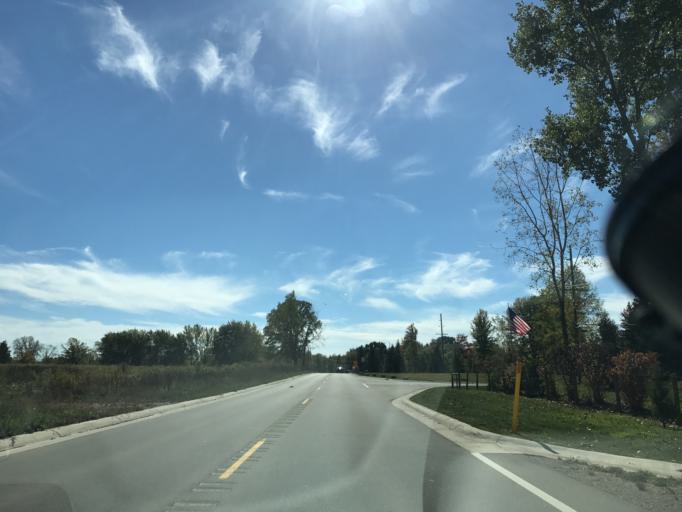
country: US
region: Michigan
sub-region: Oakland County
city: South Lyon
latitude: 42.4361
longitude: -83.6300
